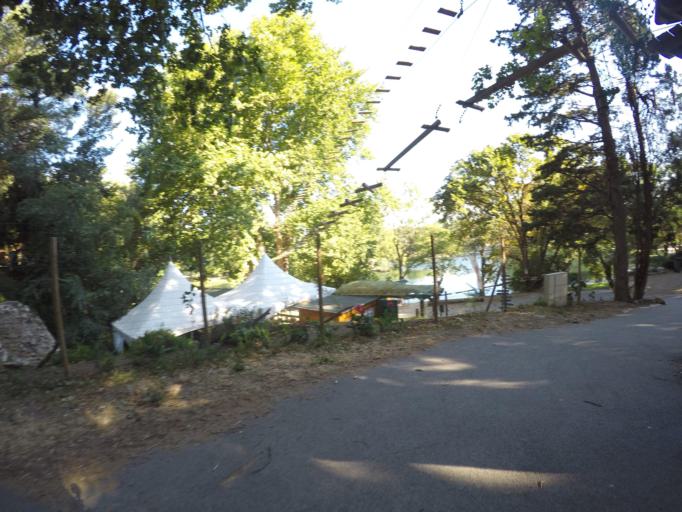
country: FR
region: Languedoc-Roussillon
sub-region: Departement des Pyrenees-Orientales
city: Le Soler
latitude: 42.6825
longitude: 2.7885
